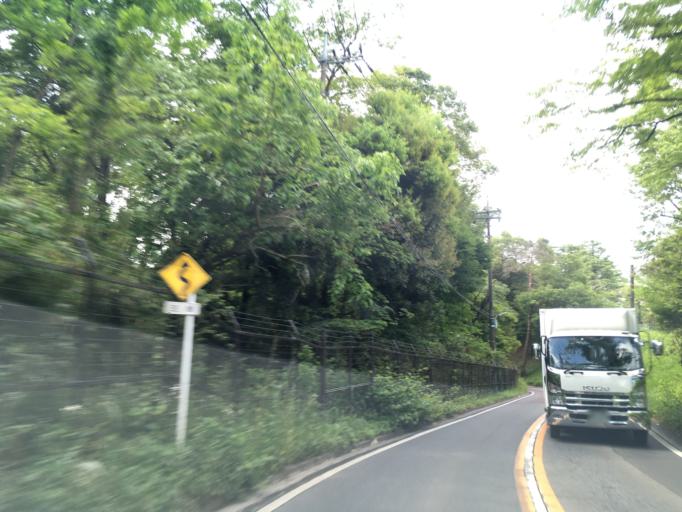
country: JP
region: Saitama
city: Tokorozawa
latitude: 35.7831
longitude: 139.4160
